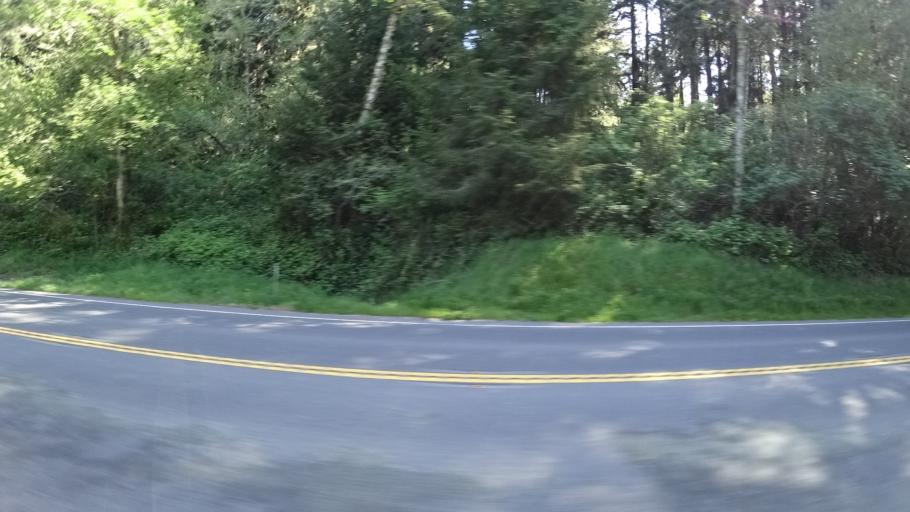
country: US
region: California
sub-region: Del Norte County
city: Bertsch-Oceanview
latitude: 41.7302
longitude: -124.1443
